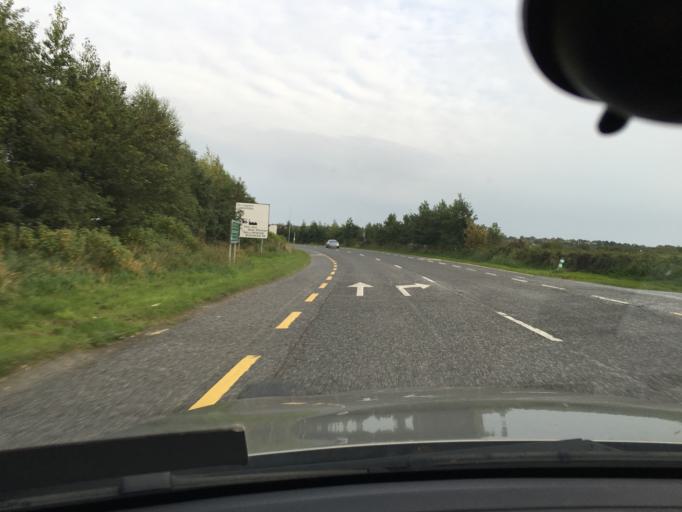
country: IE
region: Leinster
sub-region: An Longfort
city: Longford
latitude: 53.7239
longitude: -7.8224
